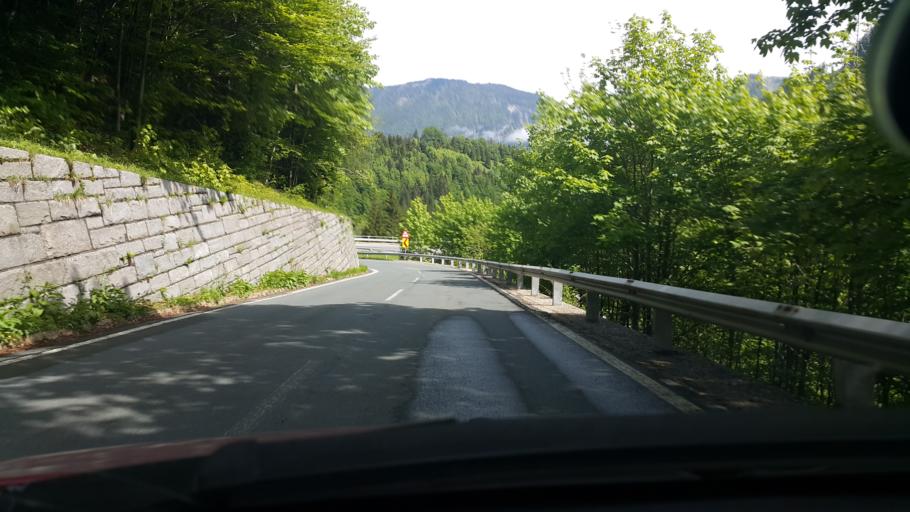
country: AT
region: Carinthia
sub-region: Politischer Bezirk Klagenfurt Land
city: Ferlach
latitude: 46.4508
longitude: 14.2555
